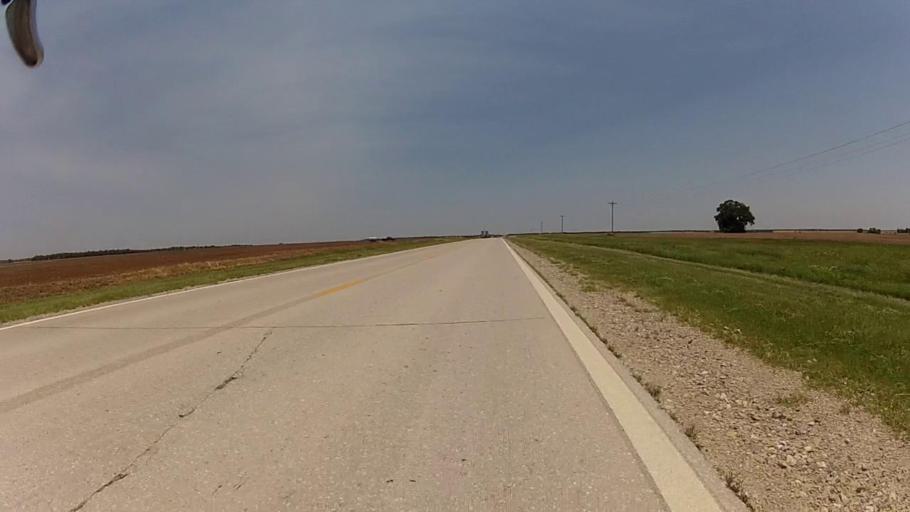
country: US
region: Kansas
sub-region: Cowley County
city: Arkansas City
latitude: 37.0575
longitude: -97.2652
